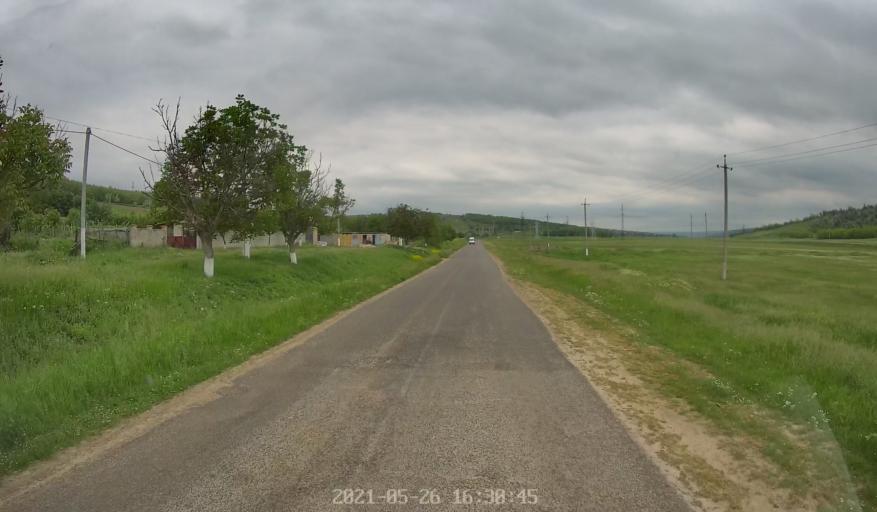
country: MD
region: Hincesti
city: Dancu
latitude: 46.8010
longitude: 28.3530
